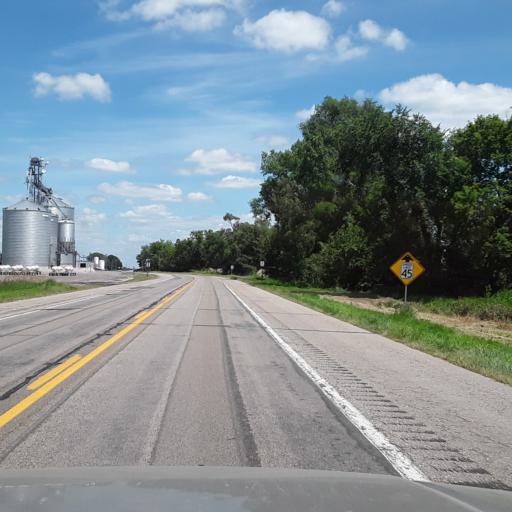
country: US
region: Nebraska
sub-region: Platte County
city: Columbus
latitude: 41.3859
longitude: -97.4987
